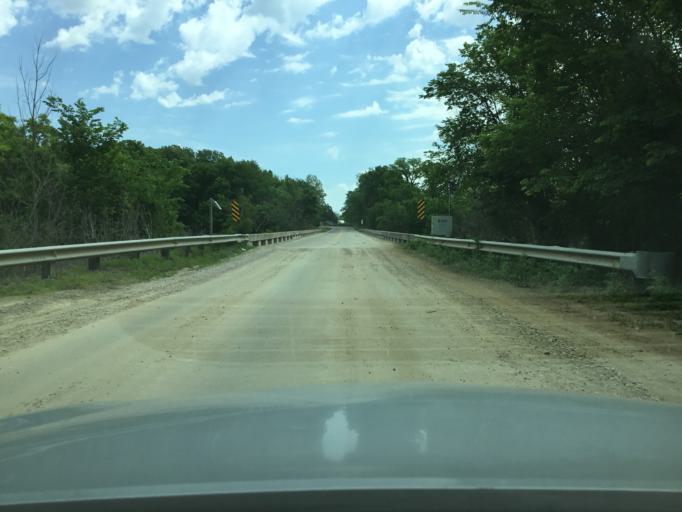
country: US
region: Kansas
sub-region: Montgomery County
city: Coffeyville
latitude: 37.0052
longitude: -95.5931
